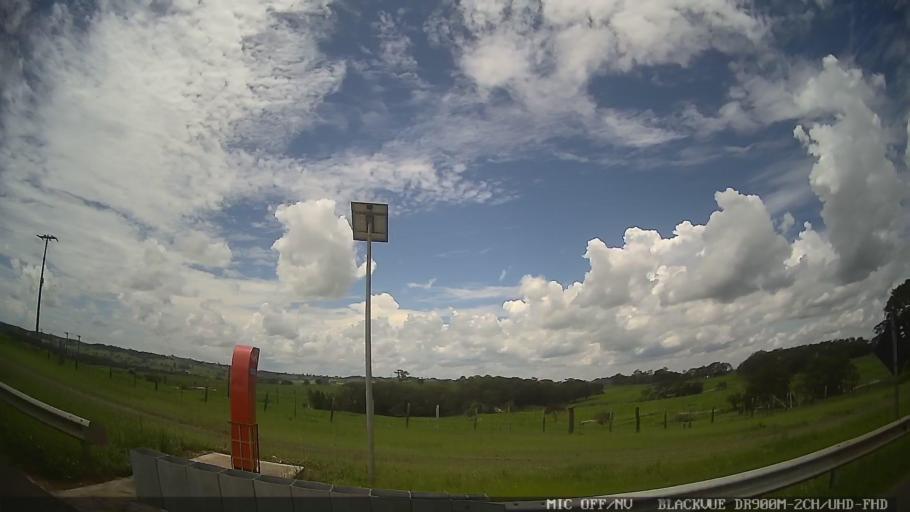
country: BR
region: Sao Paulo
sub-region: Conchas
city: Conchas
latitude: -23.0463
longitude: -47.9572
